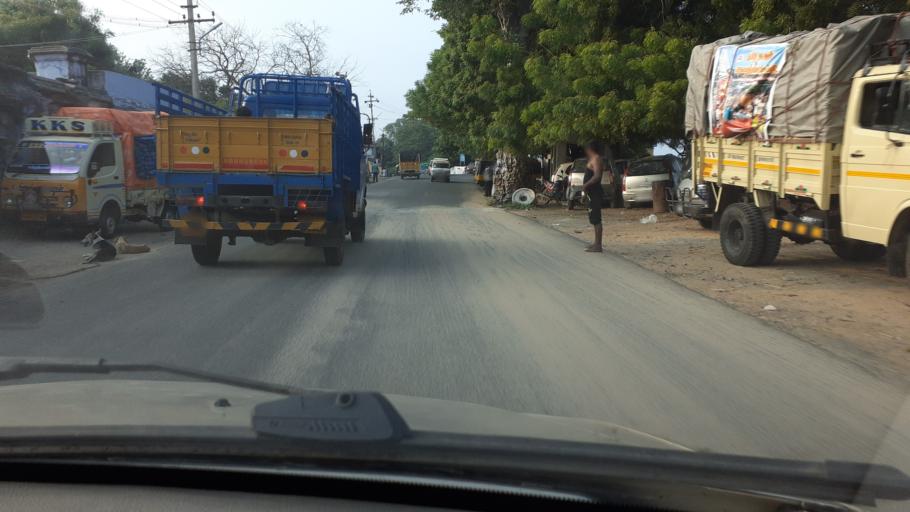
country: IN
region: Tamil Nadu
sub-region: Thoothukkudi
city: Srivaikuntam
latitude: 8.6238
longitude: 77.9094
